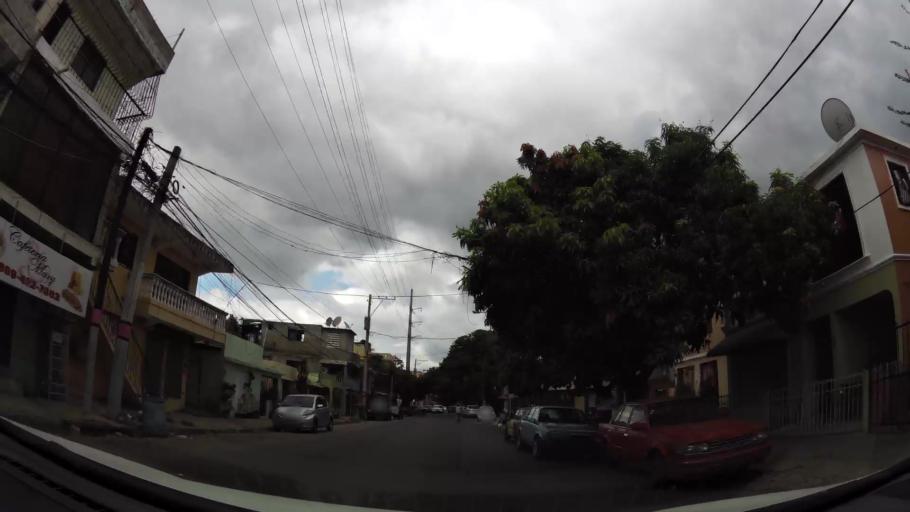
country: DO
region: Nacional
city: Bella Vista
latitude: 18.4532
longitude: -69.9325
